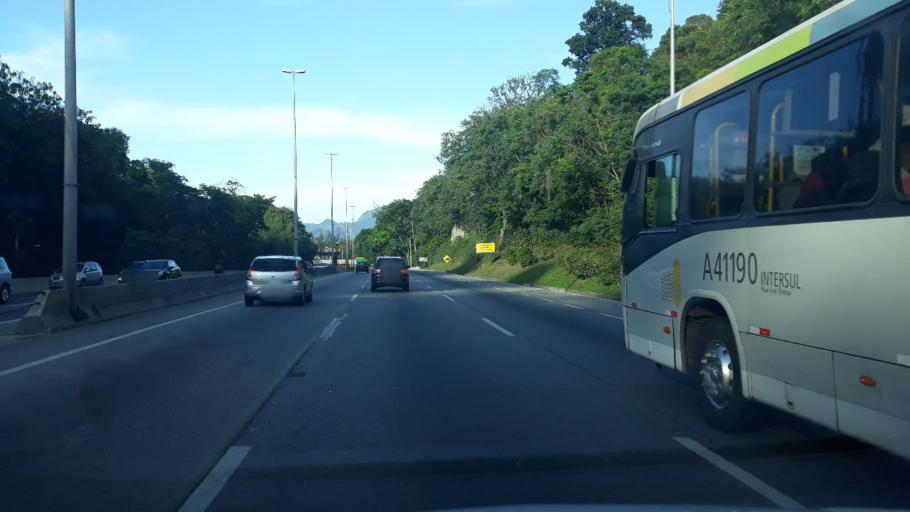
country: BR
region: Rio de Janeiro
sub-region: Sao Joao De Meriti
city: Sao Joao de Meriti
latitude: -22.9230
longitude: -43.3339
